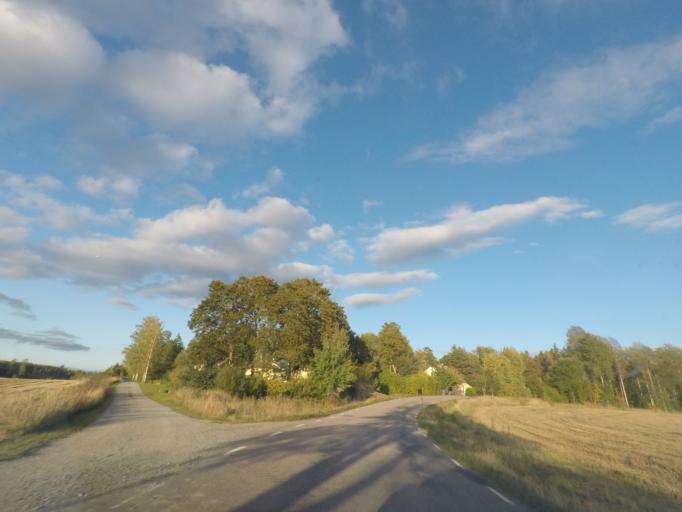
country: SE
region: Vaestmanland
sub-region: Kopings Kommun
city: Koping
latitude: 59.5099
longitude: 16.0720
